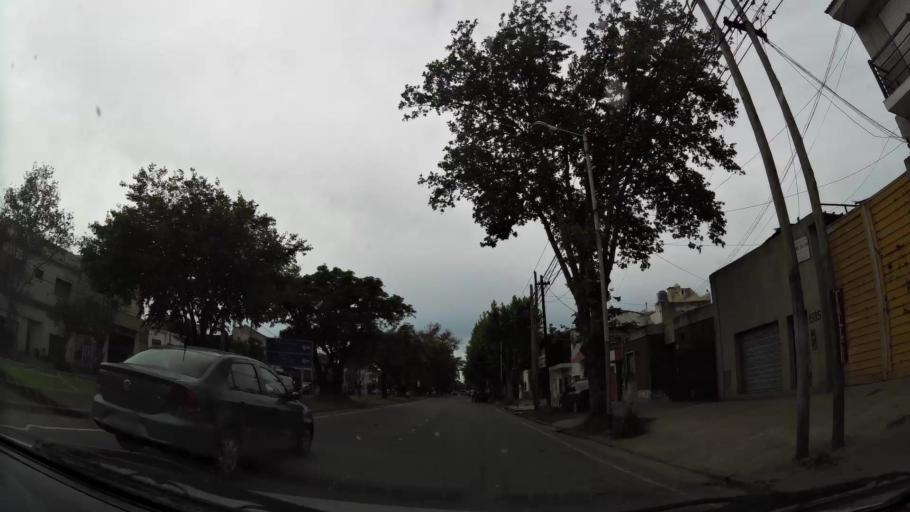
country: AR
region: Buenos Aires
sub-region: Partido de Avellaneda
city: Avellaneda
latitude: -34.6630
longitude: -58.3553
